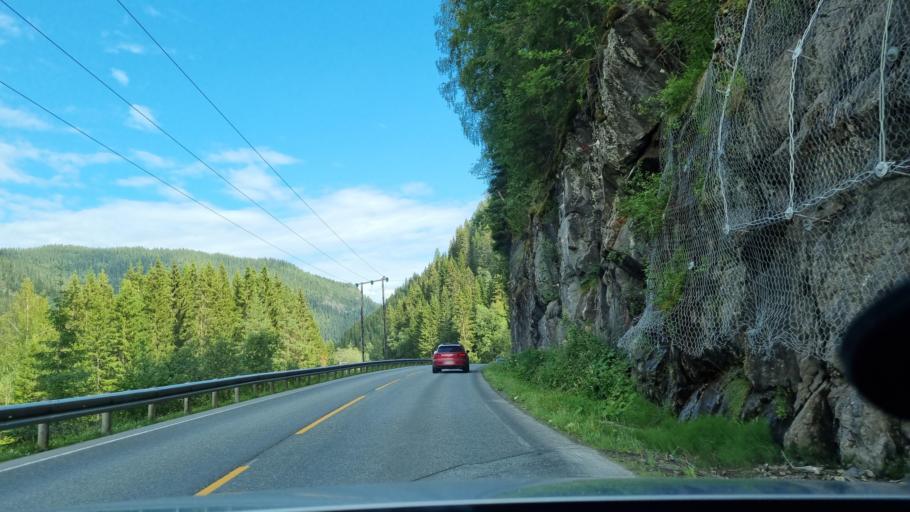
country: NO
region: Sor-Trondelag
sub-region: Midtre Gauldal
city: Storen
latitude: 62.9918
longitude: 10.5101
